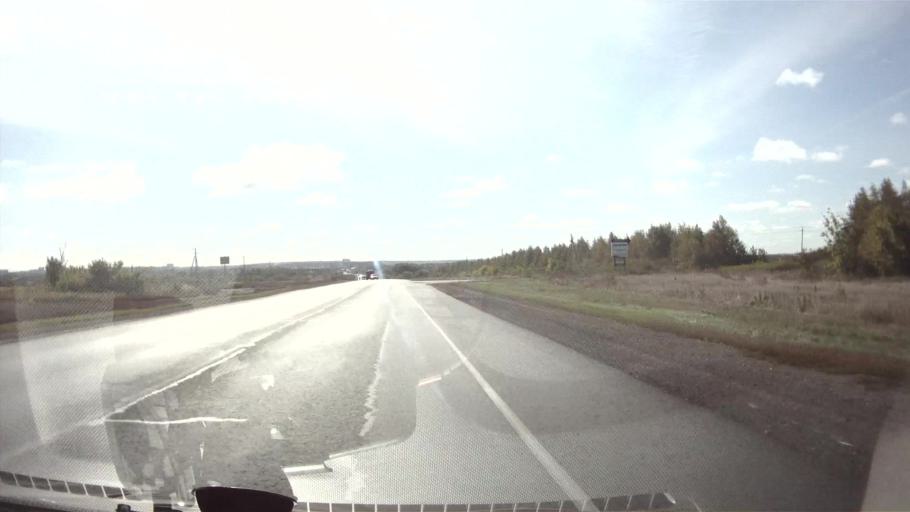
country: RU
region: Ulyanovsk
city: Isheyevka
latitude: 54.3124
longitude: 48.2352
